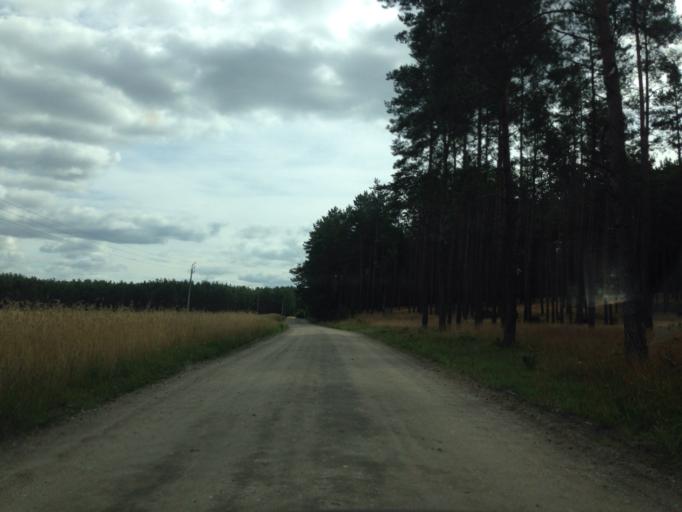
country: PL
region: Pomeranian Voivodeship
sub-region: Powiat koscierski
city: Lipusz
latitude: 54.0742
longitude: 17.6987
